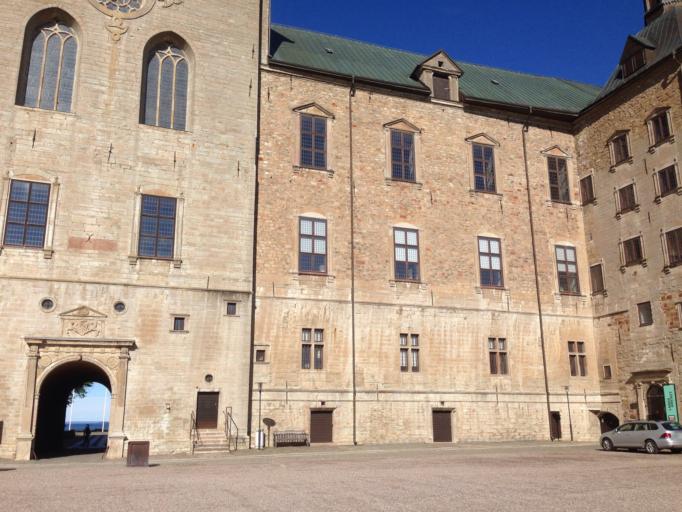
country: SE
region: OEstergoetland
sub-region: Vadstena Kommun
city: Vadstena
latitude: 58.4461
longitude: 14.8835
